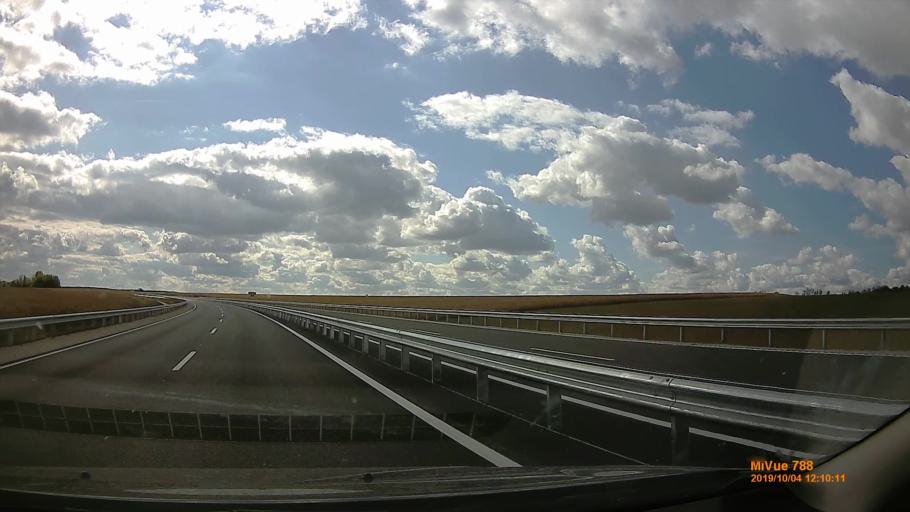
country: HU
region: Somogy
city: Kaposvar
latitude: 46.5097
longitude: 17.8089
